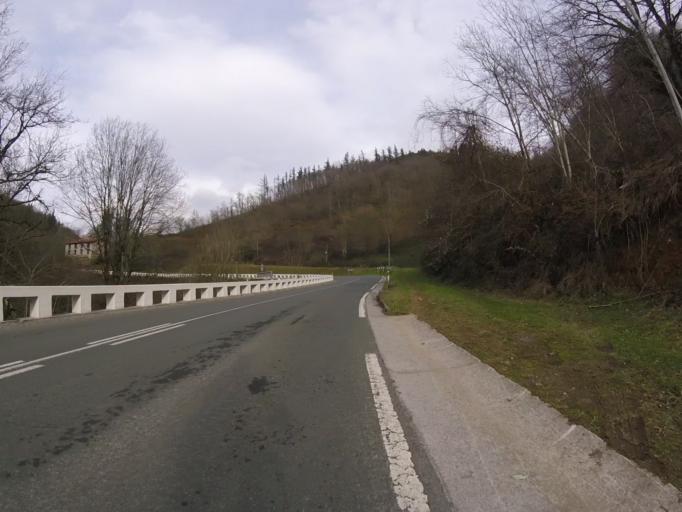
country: ES
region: Basque Country
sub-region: Provincia de Guipuzcoa
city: Albiztur
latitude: 43.1243
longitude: -2.1547
